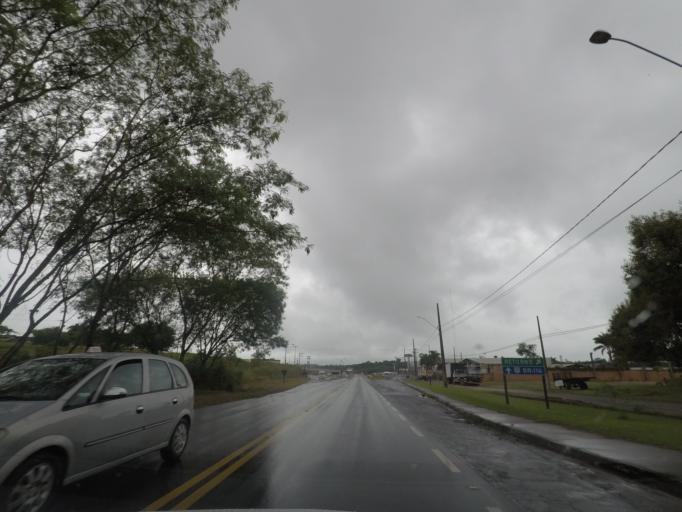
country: BR
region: Sao Paulo
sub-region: Registro
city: Registro
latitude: -24.5058
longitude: -47.8520
